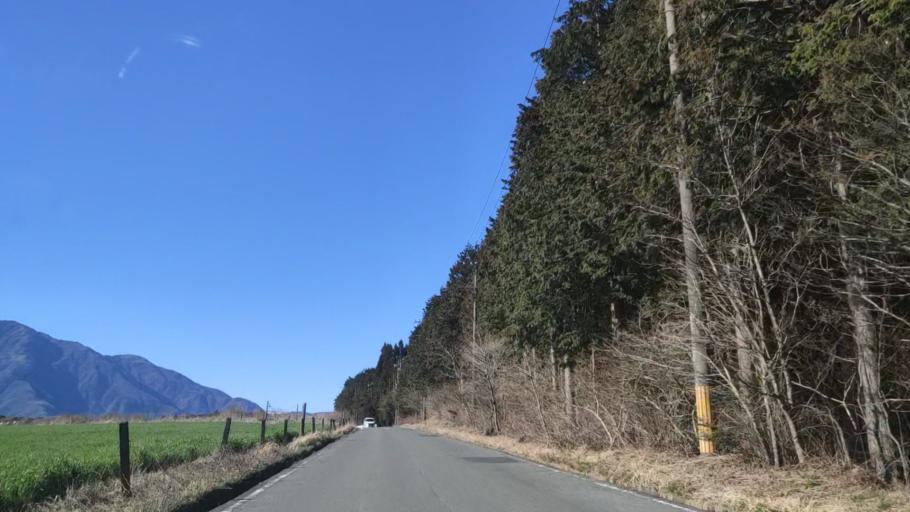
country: JP
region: Yamanashi
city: Fujikawaguchiko
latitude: 35.3789
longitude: 138.6049
